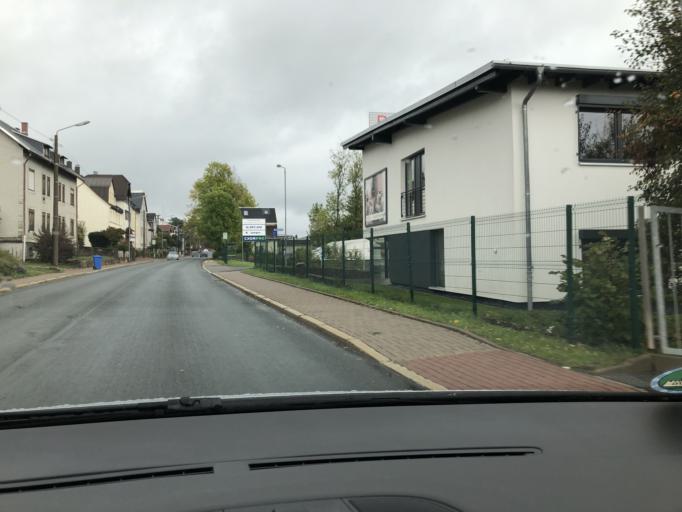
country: DE
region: Thuringia
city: Neuhaus
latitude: 50.6789
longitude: 10.9367
